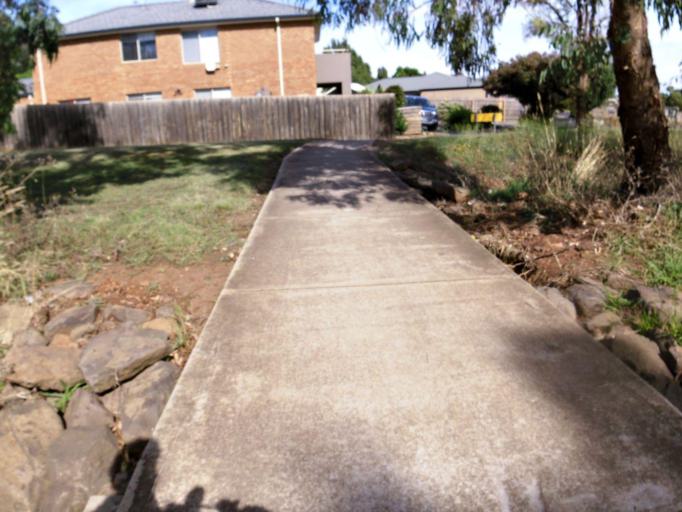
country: AU
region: Victoria
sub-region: Melton
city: Melton West
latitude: -37.6652
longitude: 144.5675
